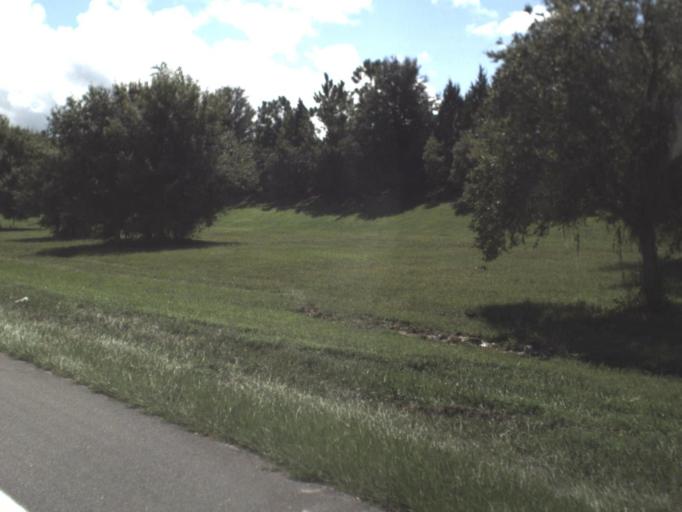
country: US
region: Florida
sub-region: Sarasota County
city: The Meadows
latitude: 27.4305
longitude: -82.3823
